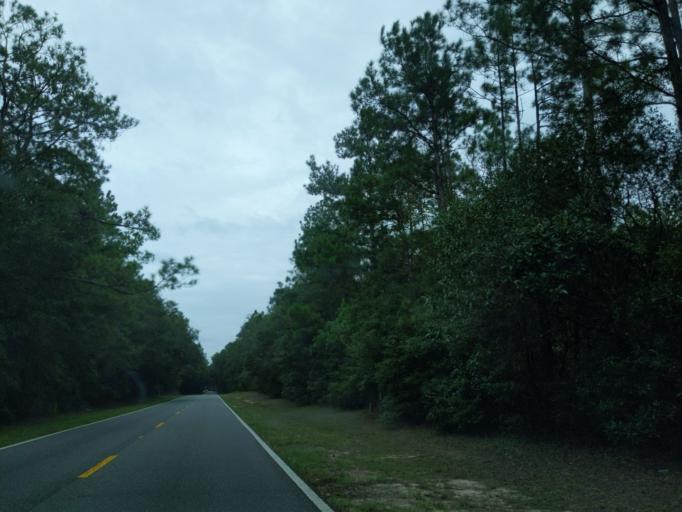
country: US
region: Florida
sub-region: Leon County
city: Woodville
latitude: 30.3674
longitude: -84.1560
